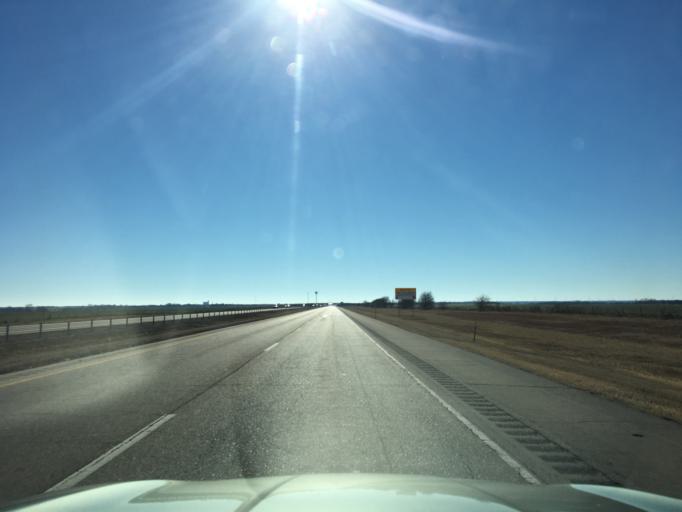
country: US
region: Oklahoma
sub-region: Kay County
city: Blackwell
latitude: 36.9666
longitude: -97.3458
